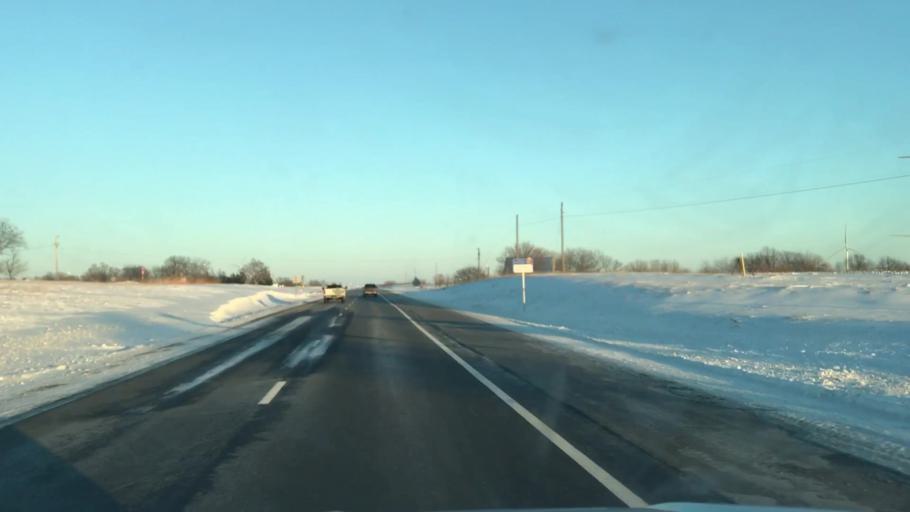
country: US
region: Missouri
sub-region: DeKalb County
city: Maysville
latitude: 39.7615
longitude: -94.4123
